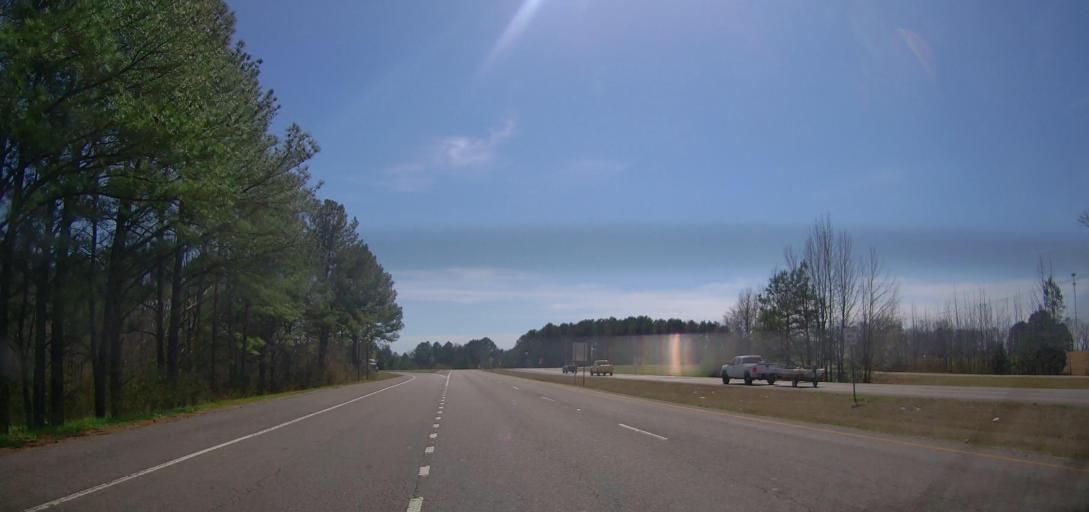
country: US
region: Alabama
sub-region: Cullman County
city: Cullman
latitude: 34.1860
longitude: -86.7848
